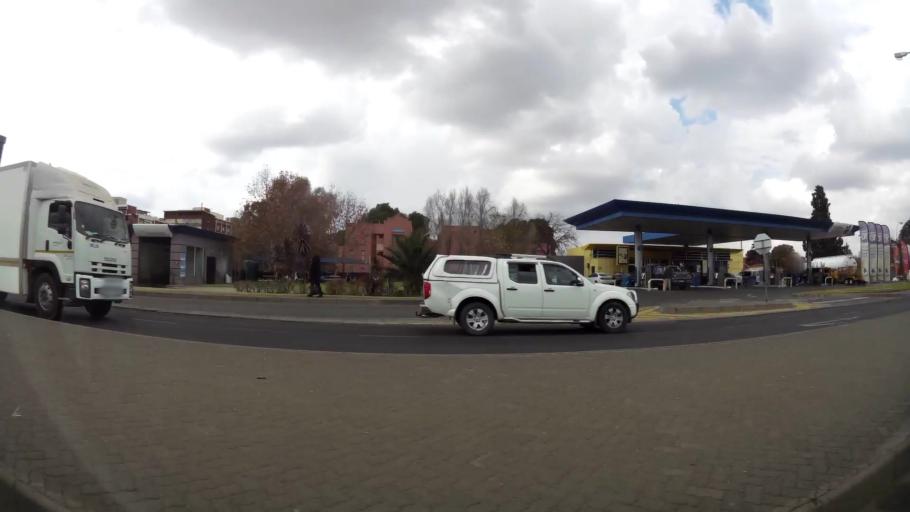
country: ZA
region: Orange Free State
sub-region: Mangaung Metropolitan Municipality
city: Bloemfontein
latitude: -29.1182
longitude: 26.2109
